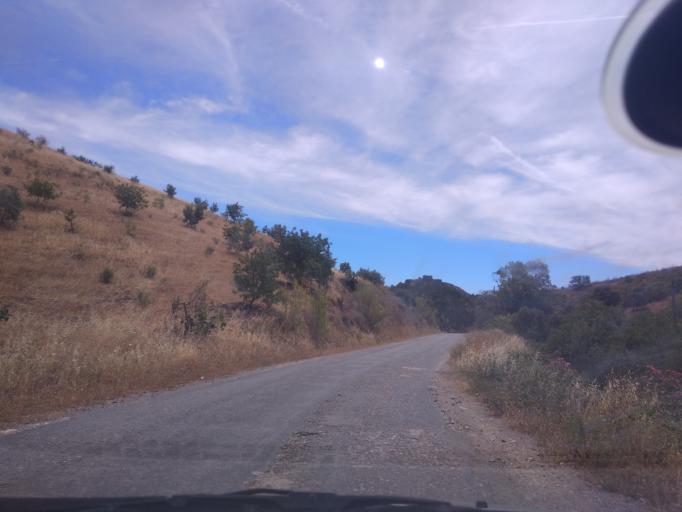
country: PT
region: Faro
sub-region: Olhao
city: Moncarapacho
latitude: 37.1654
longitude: -7.8009
